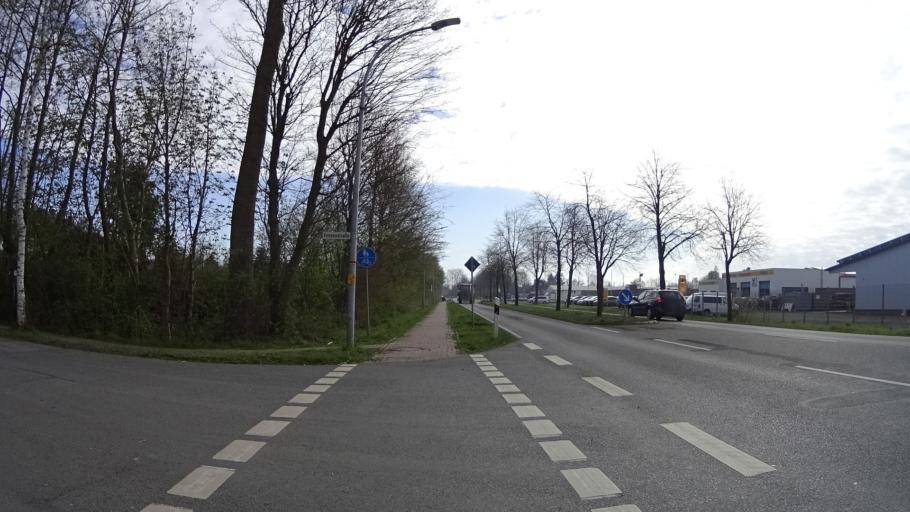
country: DE
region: Lower Saxony
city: Upgant-Schott
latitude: 53.3955
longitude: 7.3384
